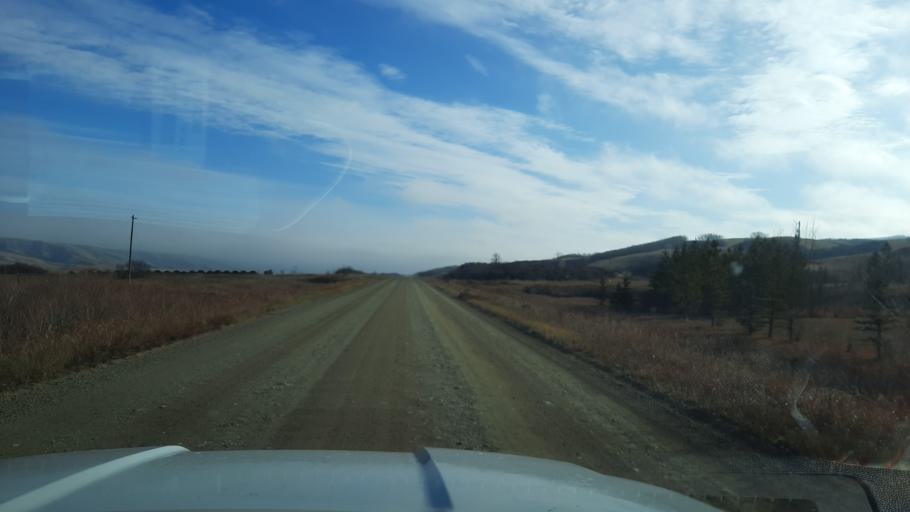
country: CA
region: Saskatchewan
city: Pilot Butte
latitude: 50.7836
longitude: -104.2491
